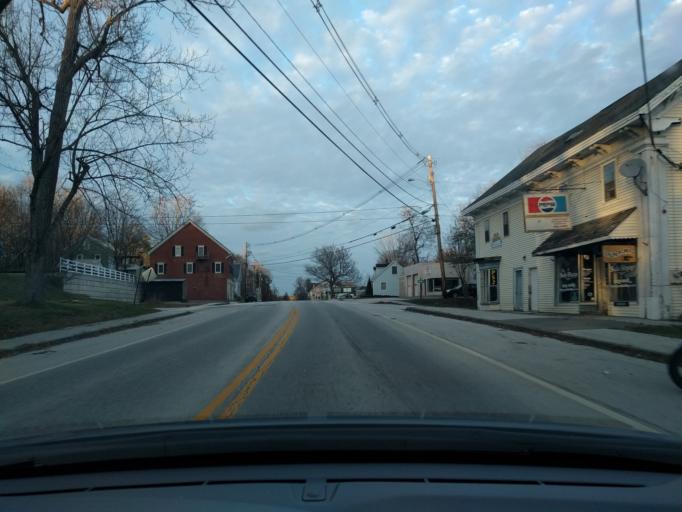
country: US
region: Maine
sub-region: Waldo County
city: Winterport
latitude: 44.6363
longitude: -68.8459
